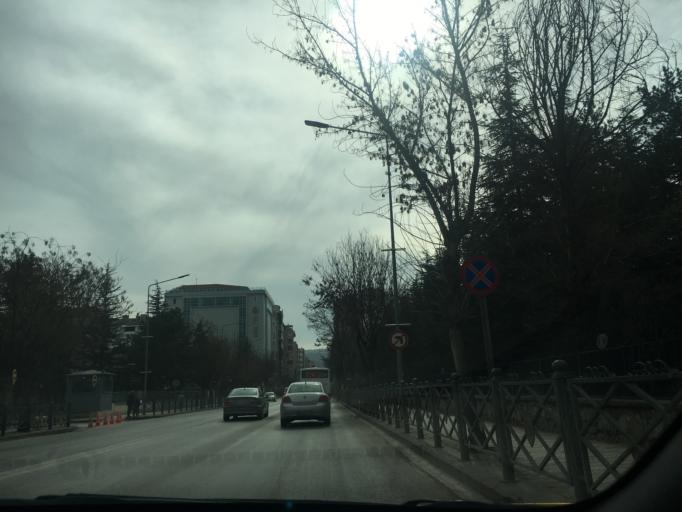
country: TR
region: Eskisehir
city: Eskisehir
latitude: 39.7705
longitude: 30.5160
